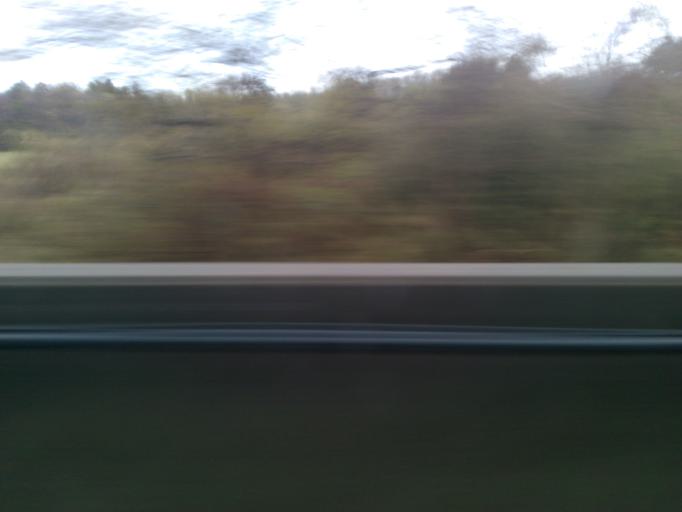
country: JP
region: Miyagi
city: Furukawa
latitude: 38.6718
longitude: 141.0282
